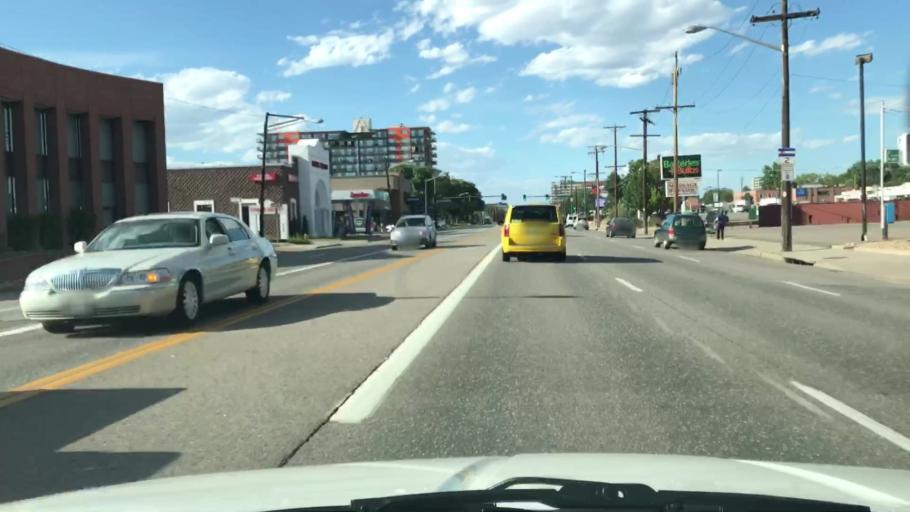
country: US
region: Colorado
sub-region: Arapahoe County
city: Cherry Hills Village
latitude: 39.6687
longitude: -104.9407
